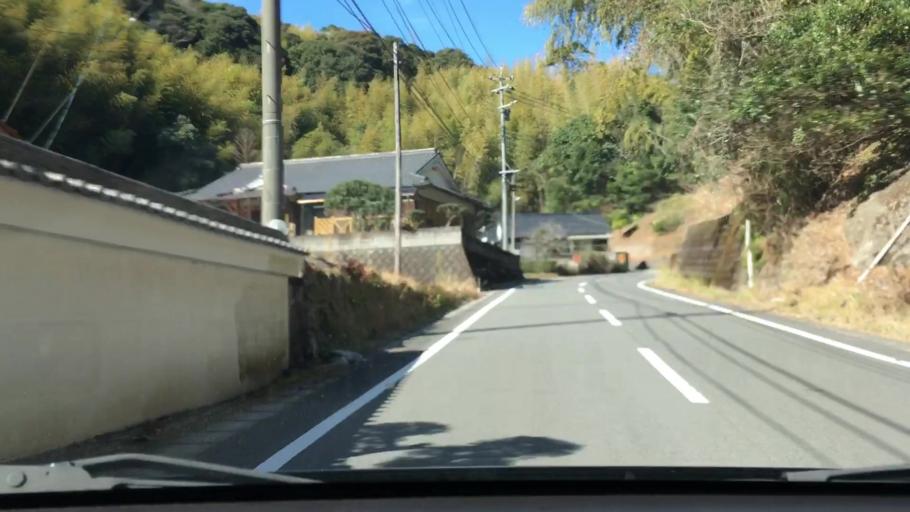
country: JP
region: Kagoshima
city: Ijuin
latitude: 31.7106
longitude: 130.4387
